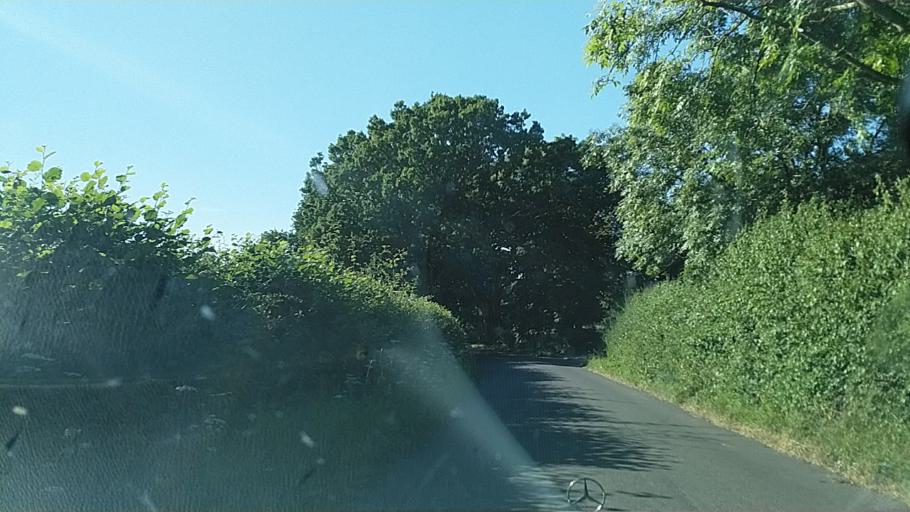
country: GB
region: England
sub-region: Warwickshire
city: Wroxall
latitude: 52.3127
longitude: -1.6394
